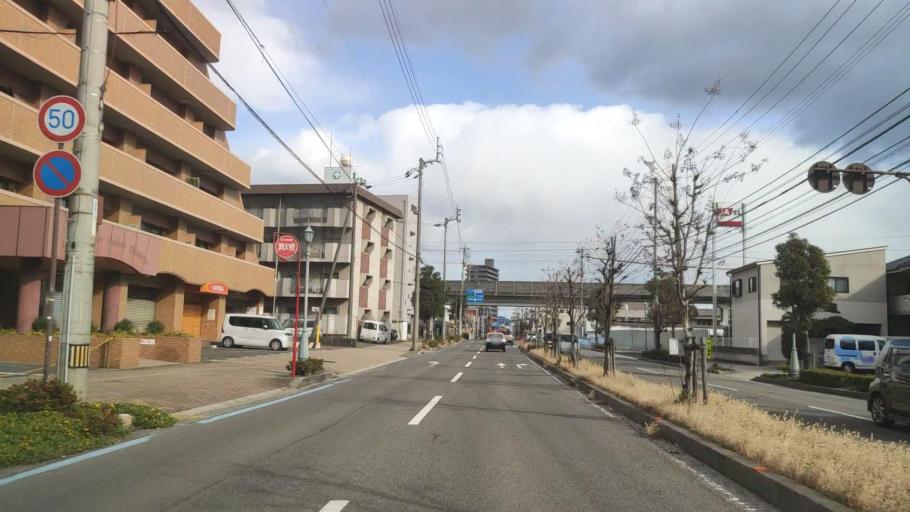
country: JP
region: Ehime
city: Hojo
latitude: 34.0660
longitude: 132.9905
